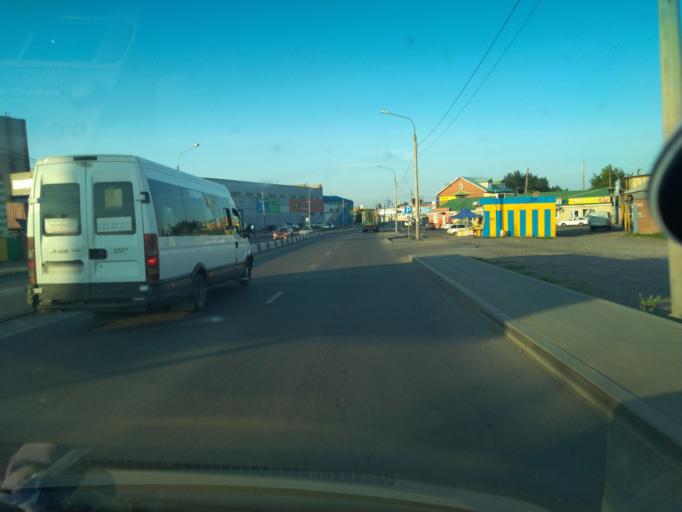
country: RU
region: Krasnoyarskiy
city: Berezovka
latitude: 56.0204
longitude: 93.0371
